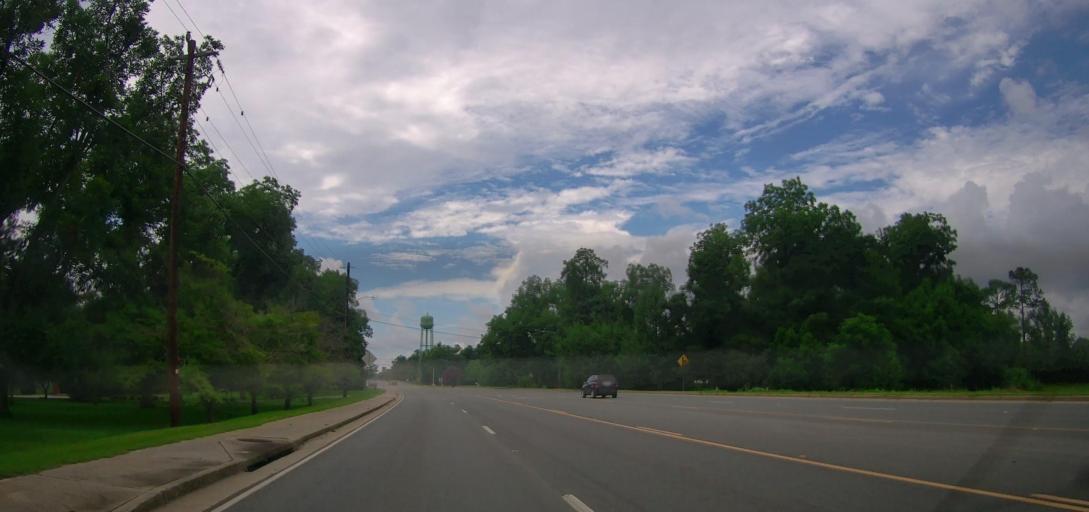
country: US
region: Georgia
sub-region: Dodge County
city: Eastman
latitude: 32.1040
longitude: -83.0620
